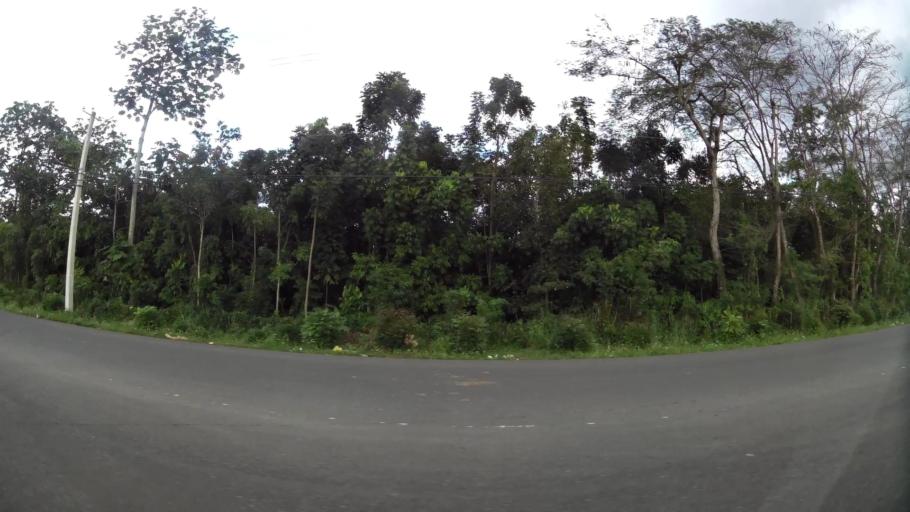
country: DO
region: Monsenor Nouel
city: Bonao
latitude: 18.9559
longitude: -70.4040
